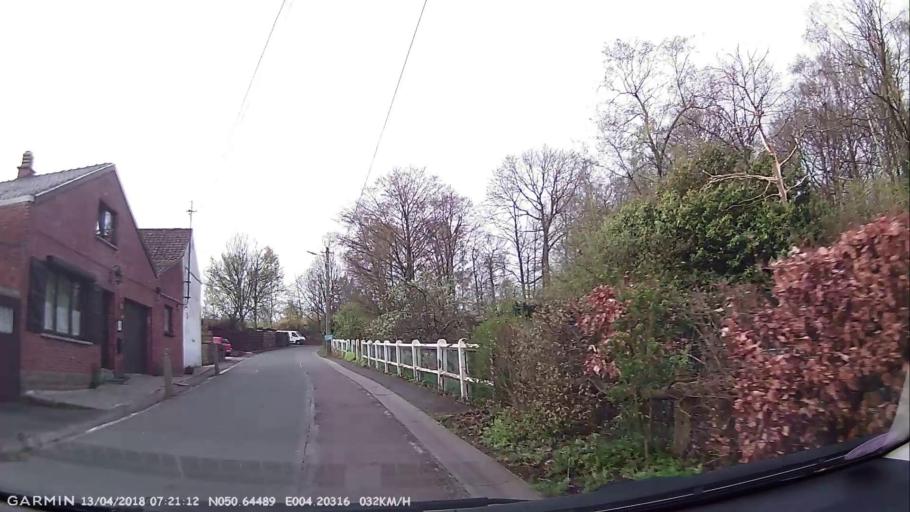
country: BE
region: Wallonia
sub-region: Province du Brabant Wallon
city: Tubize
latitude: 50.6447
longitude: 4.2031
